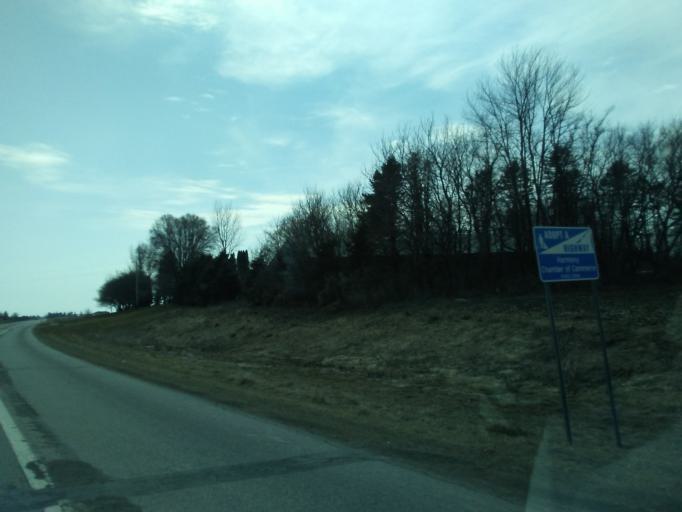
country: US
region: Minnesota
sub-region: Fillmore County
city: Harmony
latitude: 43.6075
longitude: -92.0100
